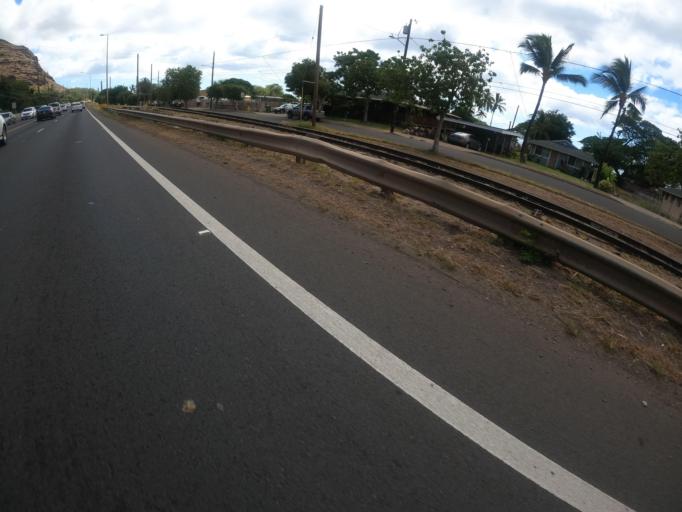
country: US
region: Hawaii
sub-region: Honolulu County
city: Nanakuli
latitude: 21.3719
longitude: -158.1391
